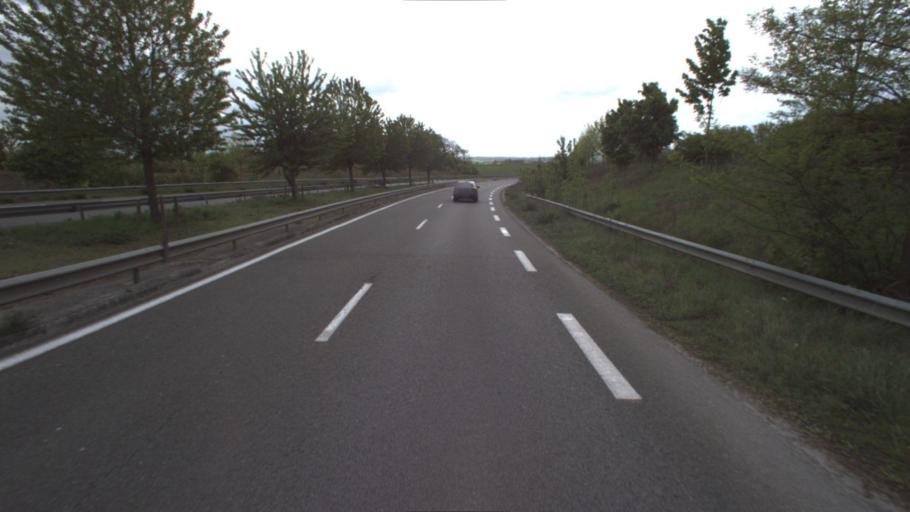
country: FR
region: Ile-de-France
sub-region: Departement de Seine-et-Marne
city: Villenoy
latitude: 48.9460
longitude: 2.8542
